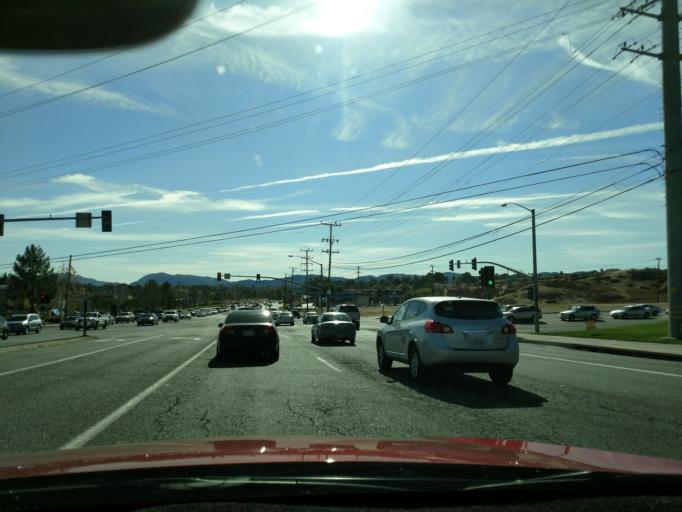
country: US
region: California
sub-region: Riverside County
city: Murrieta Hot Springs
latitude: 33.5532
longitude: -117.1404
